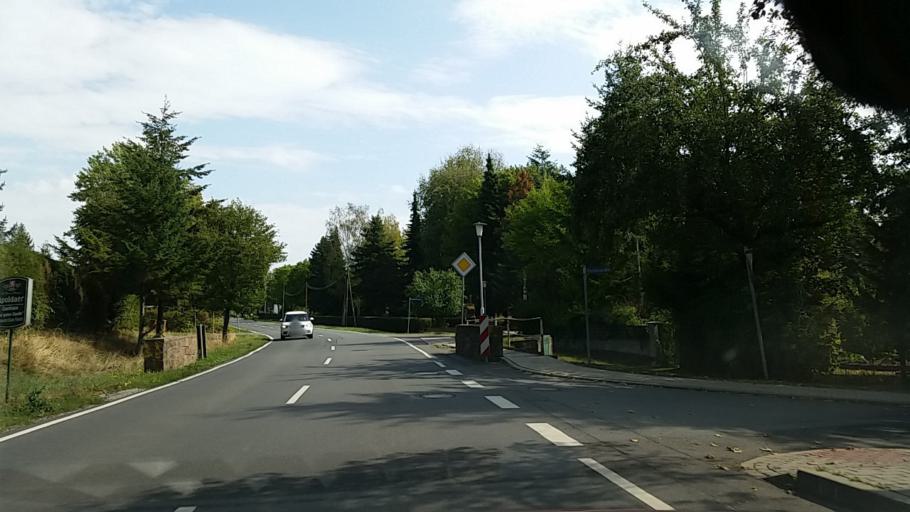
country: DE
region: Thuringia
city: Rossleben
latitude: 51.3342
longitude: 11.4674
